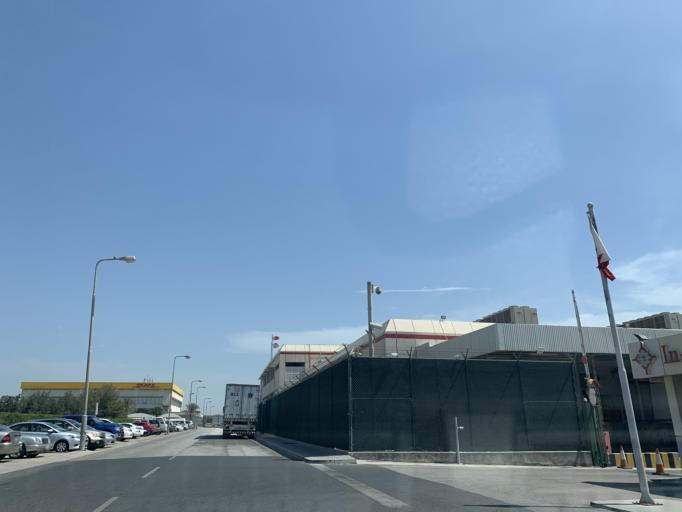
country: BH
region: Muharraq
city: Al Muharraq
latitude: 26.2701
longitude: 50.6208
